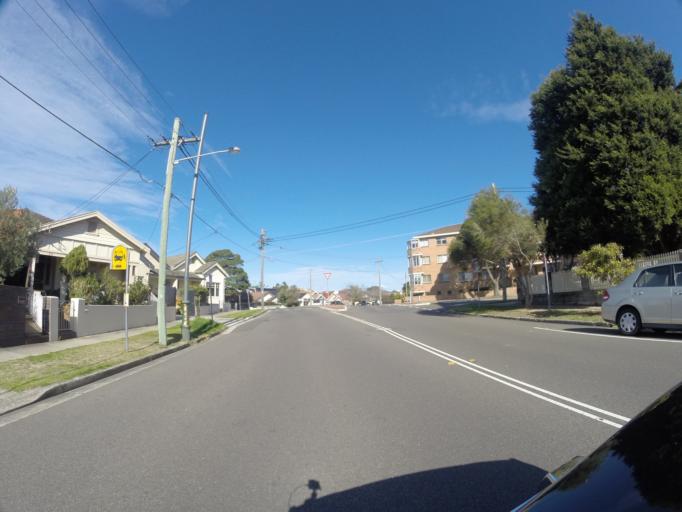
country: AU
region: New South Wales
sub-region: Randwick
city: Clovelly
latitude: -33.9078
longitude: 151.2547
